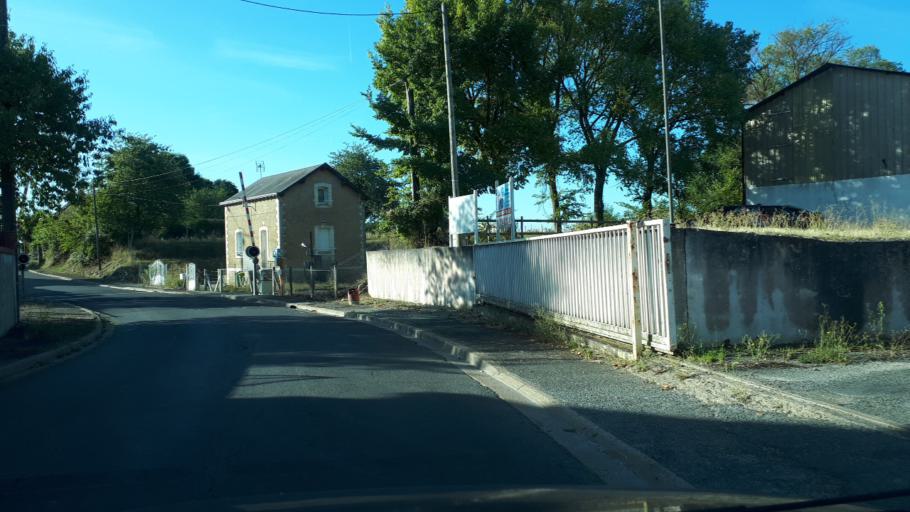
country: FR
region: Centre
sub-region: Departement d'Indre-et-Loire
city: Chateau-Renault
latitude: 47.6487
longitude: 0.9414
